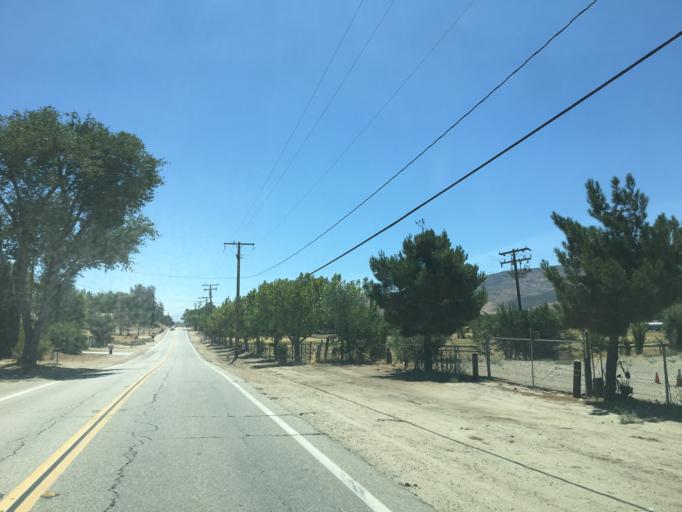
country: US
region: California
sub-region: Los Angeles County
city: Leona Valley
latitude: 34.6175
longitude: -118.2871
